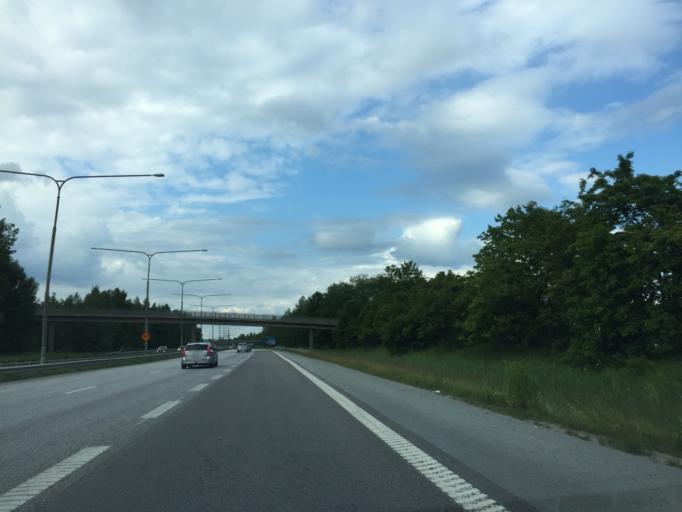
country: SE
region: OErebro
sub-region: Orebro Kommun
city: Orebro
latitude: 59.2660
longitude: 15.1741
